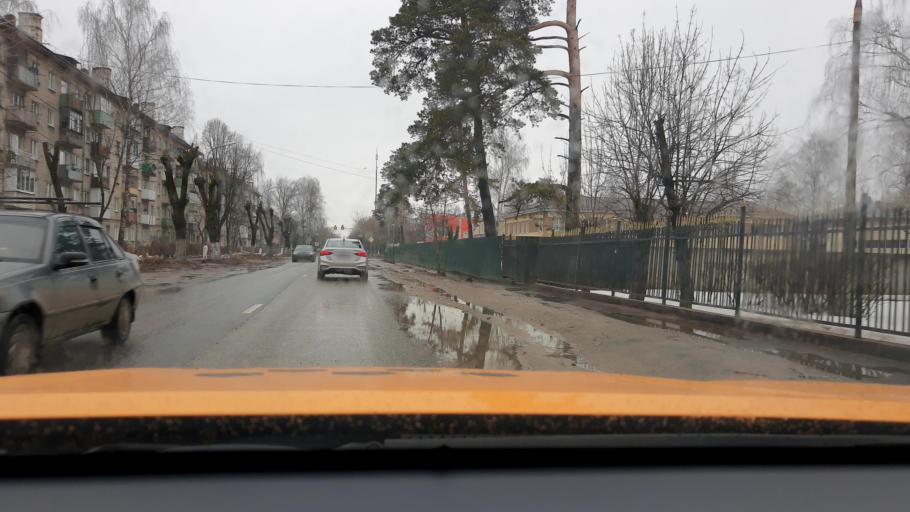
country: RU
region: Moskovskaya
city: Noginsk
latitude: 55.8852
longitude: 38.4510
